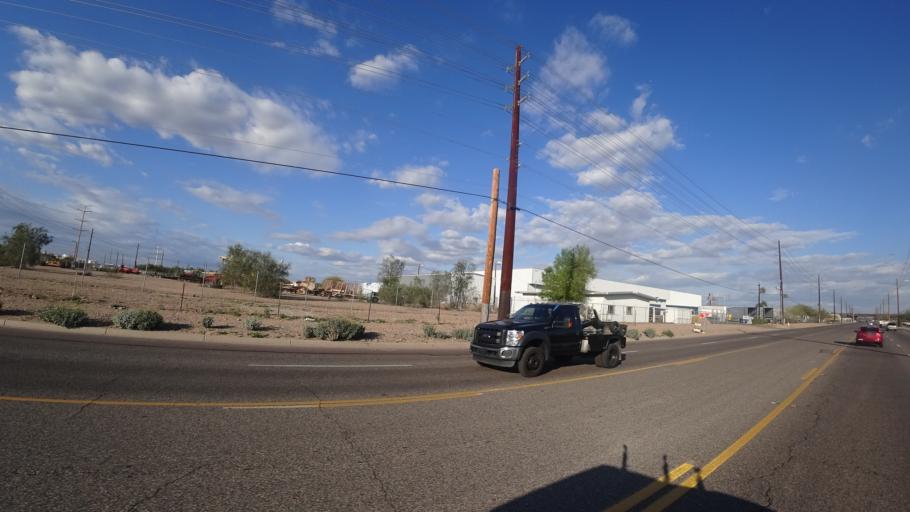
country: US
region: Arizona
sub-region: Maricopa County
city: Glendale
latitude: 33.5525
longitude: -112.2110
